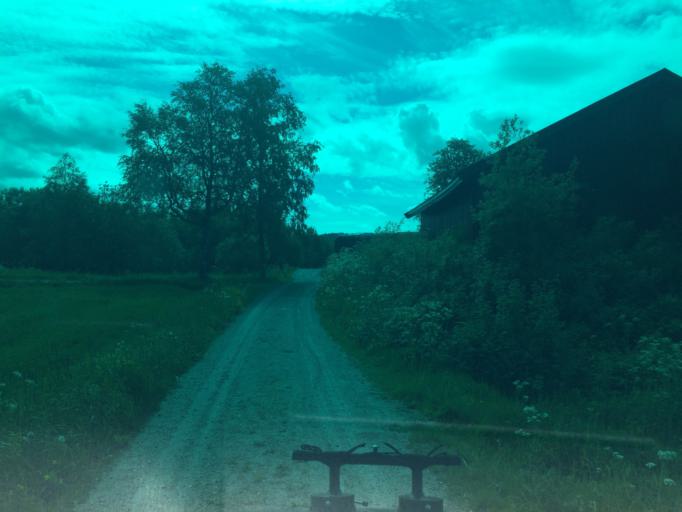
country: NO
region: Nord-Trondelag
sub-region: Overhalla
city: Ranemsletta
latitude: 64.4656
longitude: 12.0611
